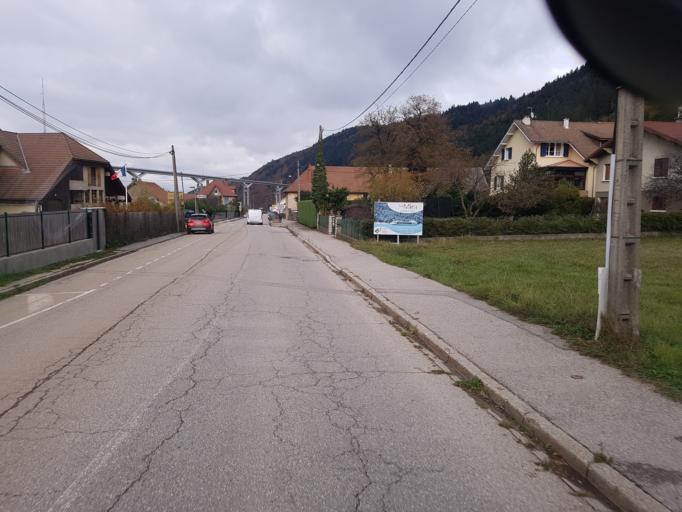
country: FR
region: Rhone-Alpes
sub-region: Departement de l'Isere
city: La Motte-Saint-Martin
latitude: 44.9240
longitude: 5.6375
